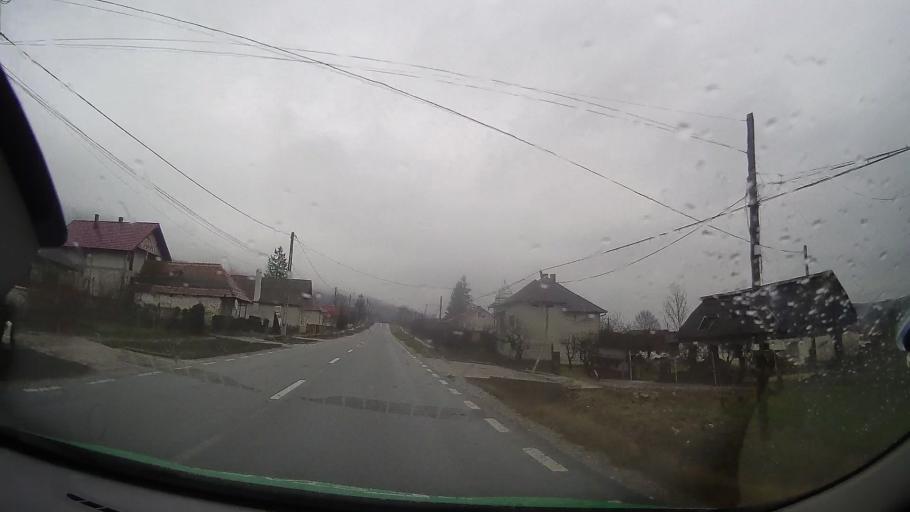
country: RO
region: Bistrita-Nasaud
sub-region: Comuna Galatii Bistritei
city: Galatii Bistritei
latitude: 46.9970
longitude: 24.4124
